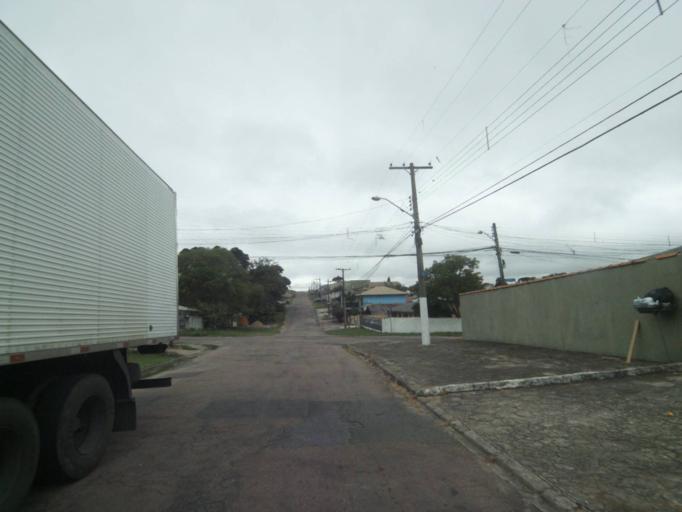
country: BR
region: Parana
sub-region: Sao Jose Dos Pinhais
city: Sao Jose dos Pinhais
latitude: -25.5412
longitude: -49.2855
